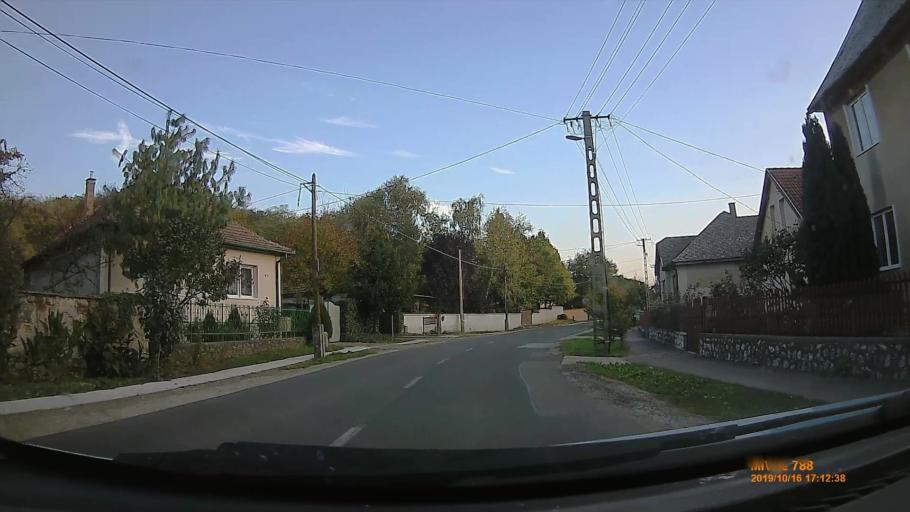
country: HU
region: Heves
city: Kerecsend
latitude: 47.8276
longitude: 20.3329
